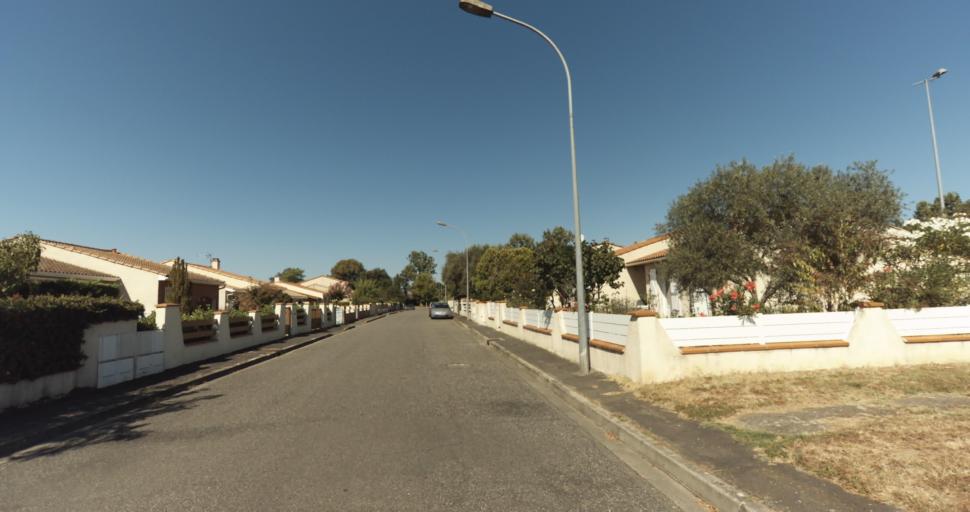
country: FR
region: Midi-Pyrenees
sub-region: Departement de la Haute-Garonne
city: L'Union
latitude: 43.6468
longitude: 1.4806
